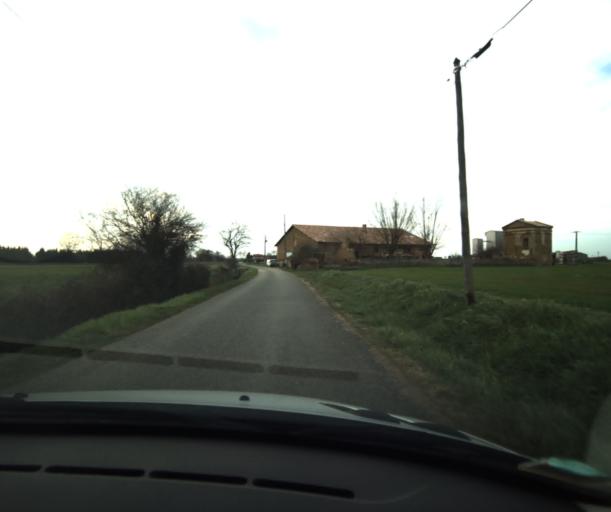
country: FR
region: Midi-Pyrenees
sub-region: Departement du Tarn-et-Garonne
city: Montech
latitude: 43.9592
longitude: 1.2159
